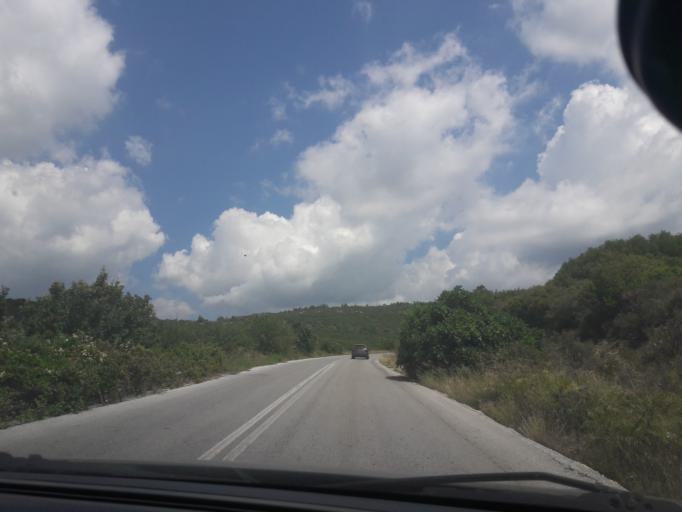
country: GR
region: Central Macedonia
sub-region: Nomos Chalkidikis
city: Polygyros
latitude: 40.3658
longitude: 23.4168
